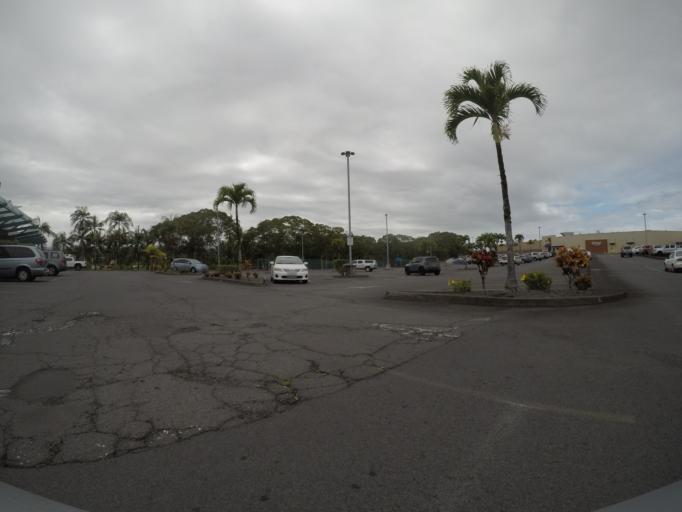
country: US
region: Hawaii
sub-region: Hawaii County
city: Hilo
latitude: 19.6957
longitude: -155.0643
